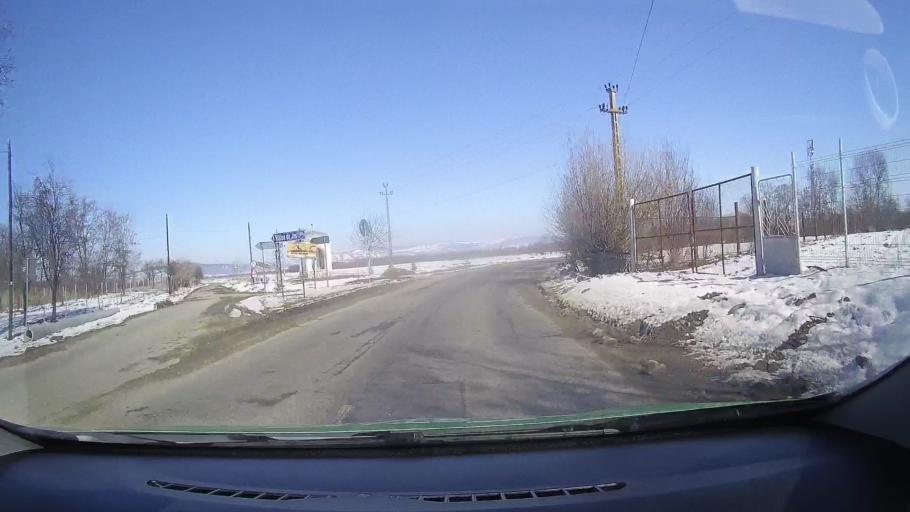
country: RO
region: Brasov
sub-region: Comuna Dragus
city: Dragus
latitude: 45.7517
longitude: 24.7391
